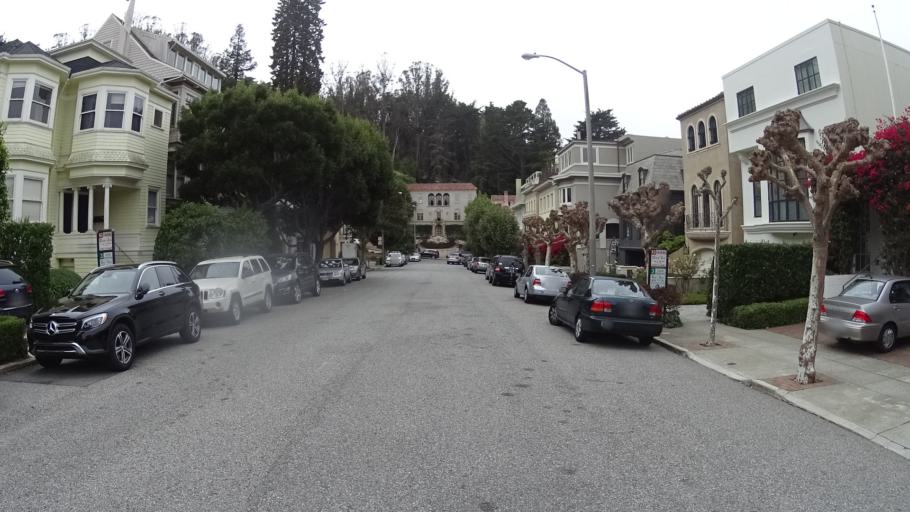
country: US
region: California
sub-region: San Francisco County
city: San Francisco
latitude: 37.7949
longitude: -122.4457
